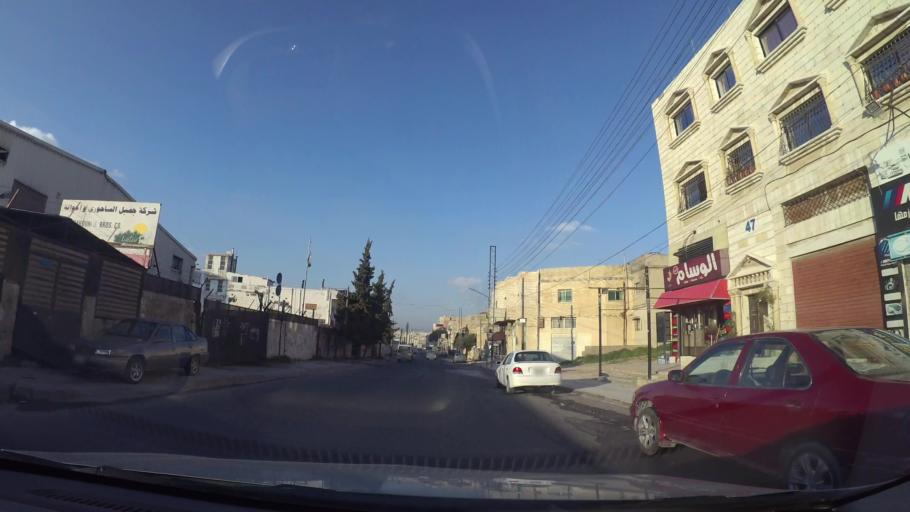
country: JO
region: Amman
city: Al Bunayyat ash Shamaliyah
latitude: 31.9085
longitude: 35.9126
